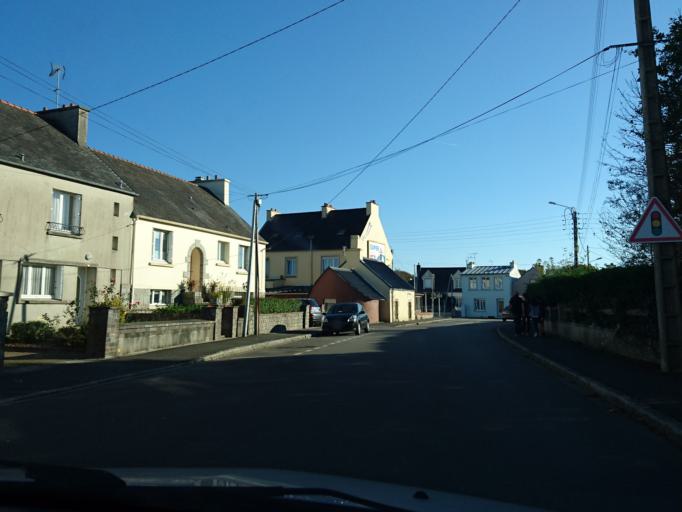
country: FR
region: Brittany
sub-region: Departement du Finistere
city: Brest
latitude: 48.4138
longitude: -4.4510
